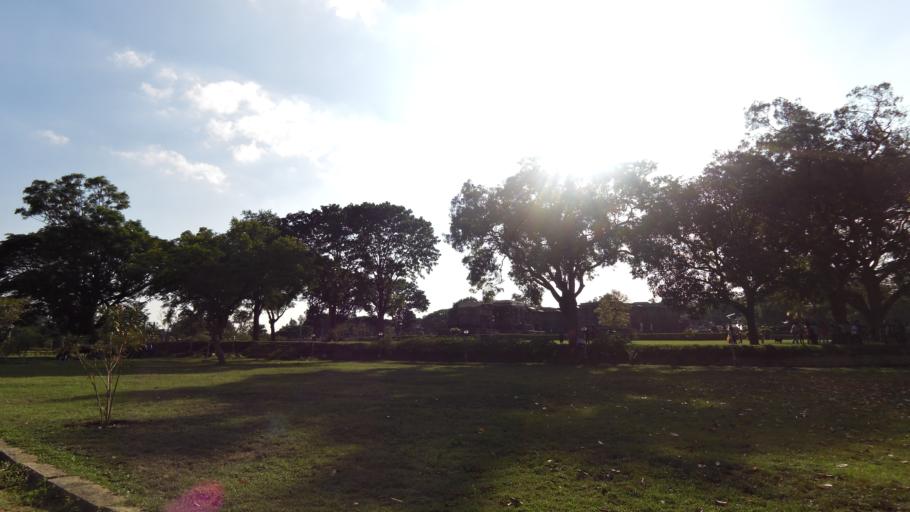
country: IN
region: Karnataka
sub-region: Hassan
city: Belur
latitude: 13.2130
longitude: 75.9952
